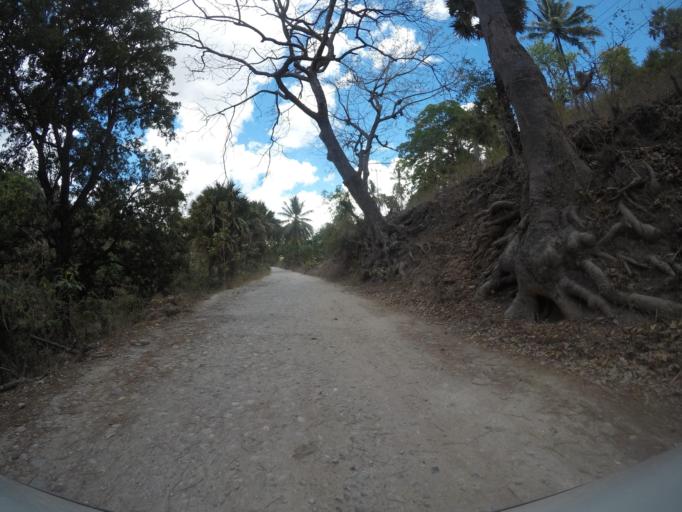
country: TL
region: Baucau
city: Baucau
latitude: -8.4843
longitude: 126.6361
